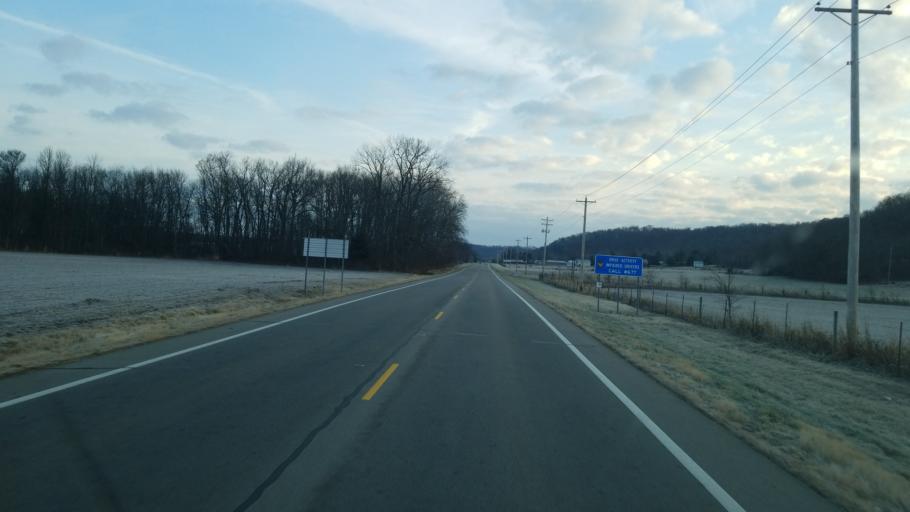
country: US
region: Ohio
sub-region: Ross County
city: North Fork Village
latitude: 39.3426
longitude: -83.0754
